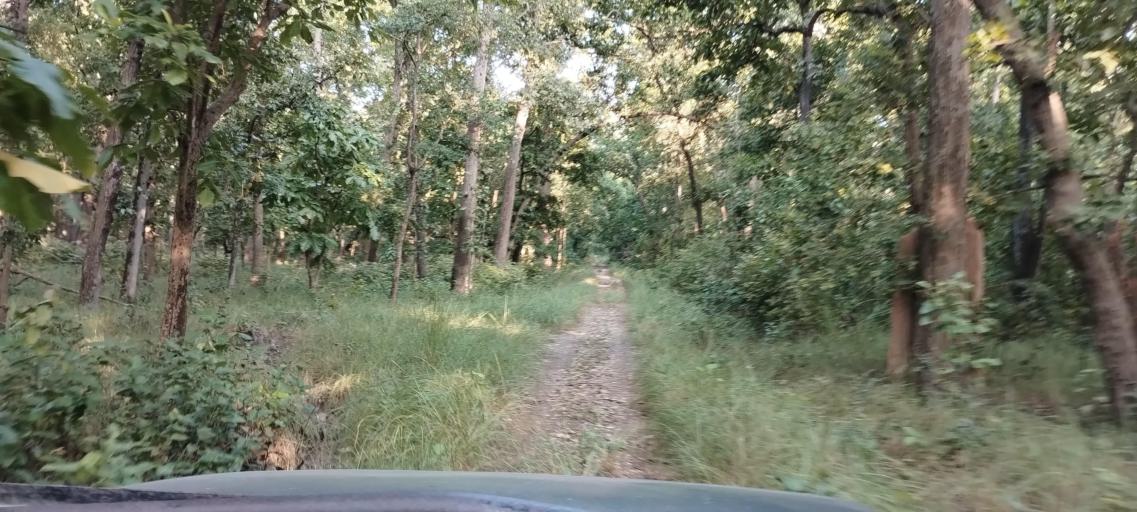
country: NP
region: Far Western
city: Tikapur
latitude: 28.4881
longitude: 81.2592
